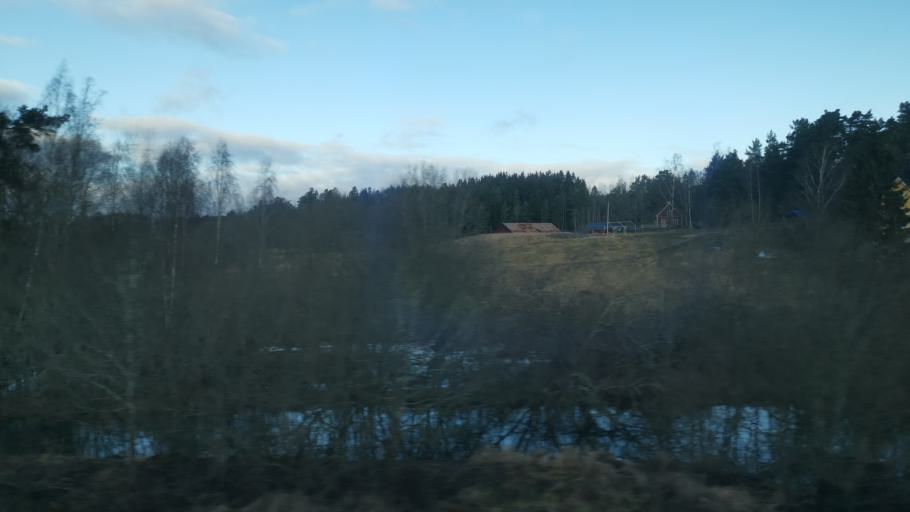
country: SE
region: Soedermanland
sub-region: Flens Kommun
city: Malmkoping
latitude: 59.0623
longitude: 16.7055
